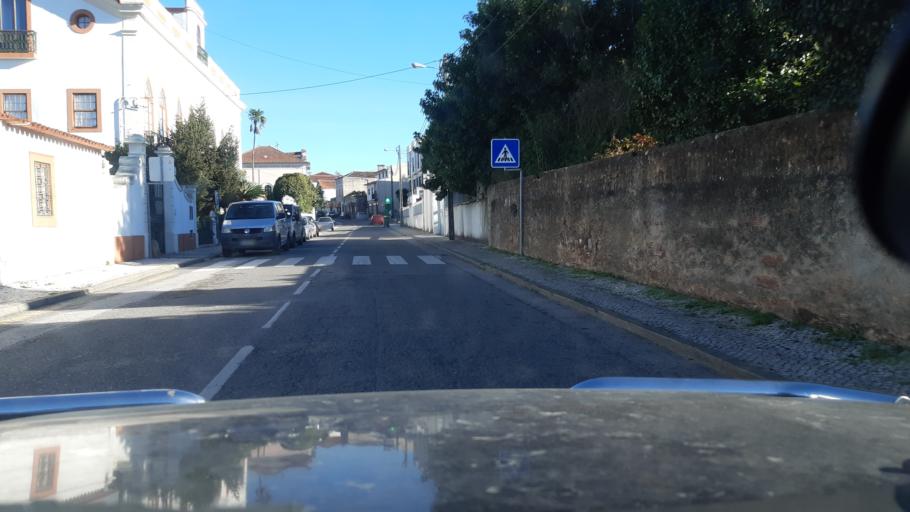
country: PT
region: Aveiro
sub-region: Agueda
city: Agueda
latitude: 40.5618
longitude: -8.4437
